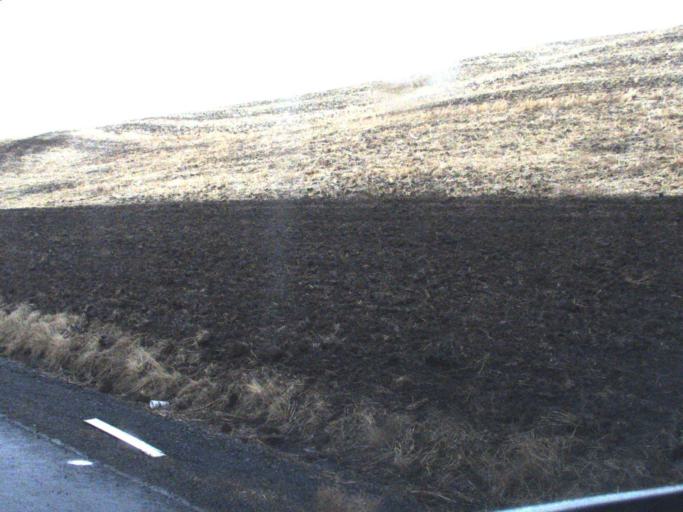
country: US
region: Washington
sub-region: Whitman County
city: Colfax
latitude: 46.9869
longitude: -117.3495
